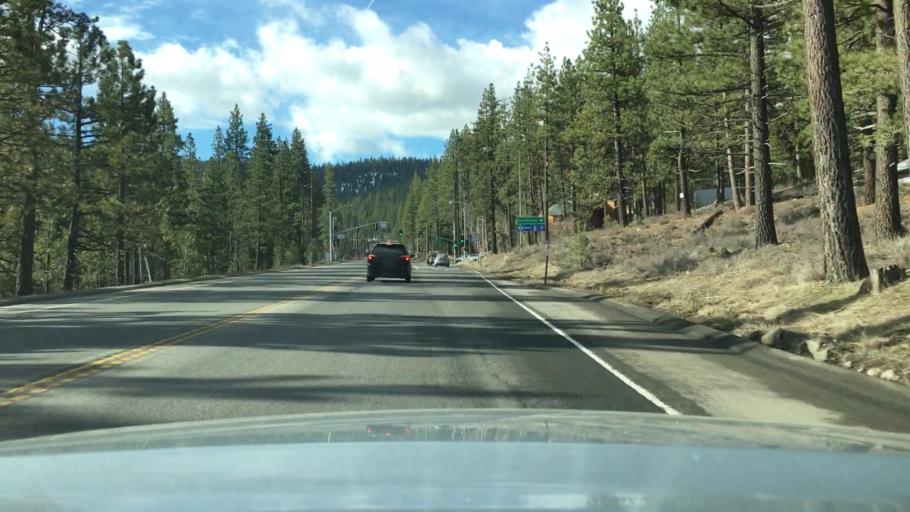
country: US
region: California
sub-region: Placer County
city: Tahoe Vista
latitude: 39.2886
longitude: -120.1037
